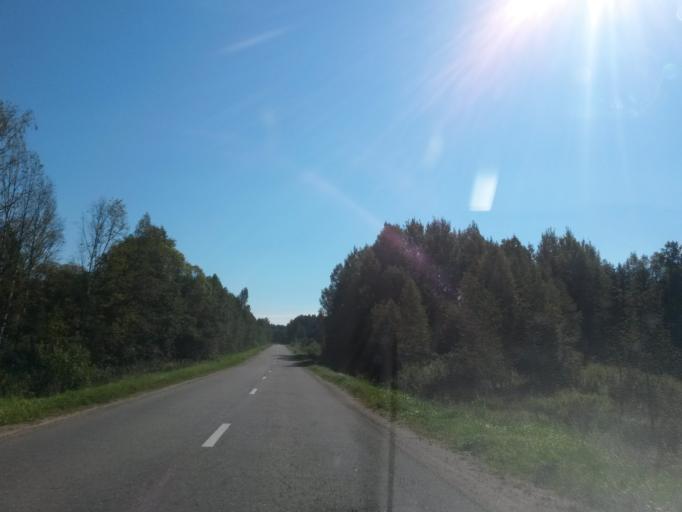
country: RU
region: Jaroslavl
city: Gavrilov-Yam
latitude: 57.3018
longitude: 40.0321
